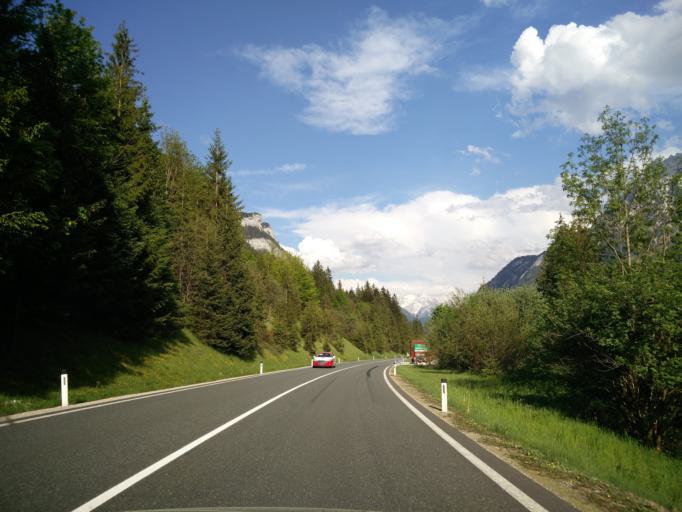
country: AT
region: Tyrol
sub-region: Politischer Bezirk Kitzbuhel
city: Waidring
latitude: 47.5875
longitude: 12.6090
